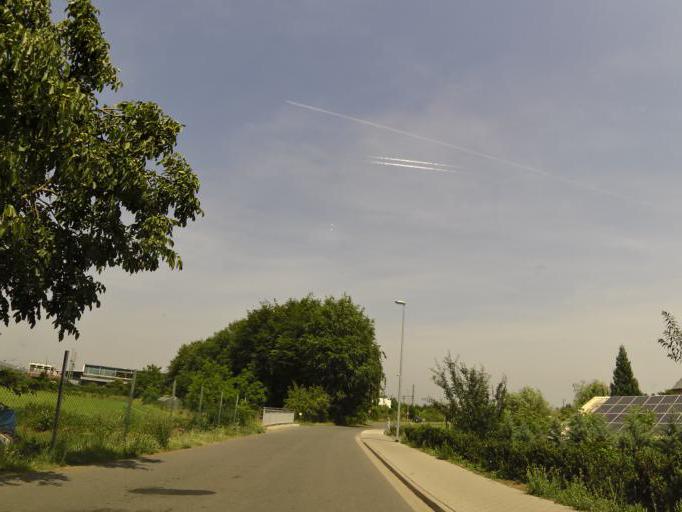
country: DE
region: Hesse
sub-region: Regierungsbezirk Darmstadt
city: Gross-Gerau
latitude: 49.9220
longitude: 8.4939
